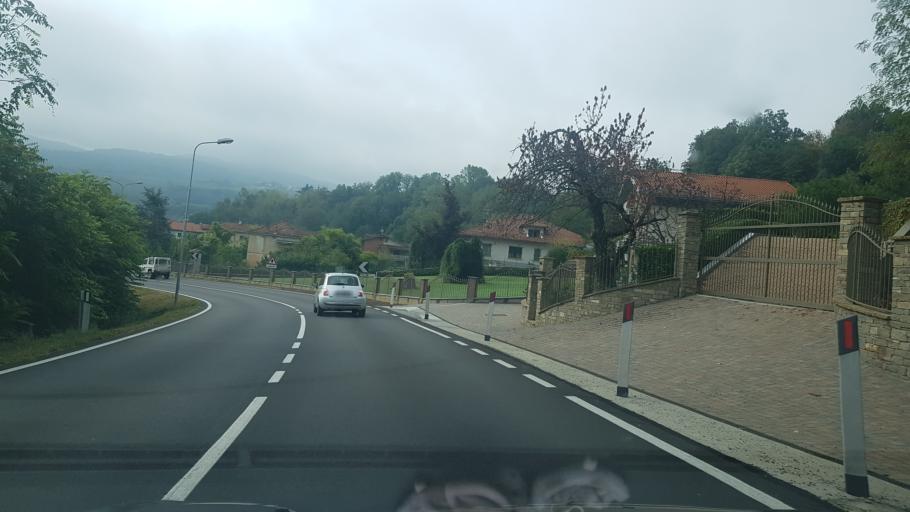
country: IT
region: Piedmont
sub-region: Provincia di Cuneo
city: Ceva
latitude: 44.3844
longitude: 8.0257
